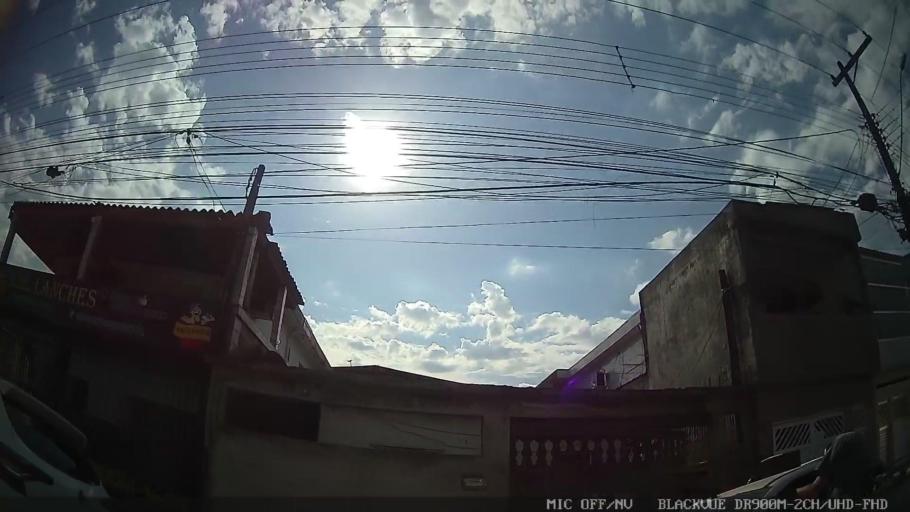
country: BR
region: Sao Paulo
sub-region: Guaruja
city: Guaruja
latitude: -23.9626
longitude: -46.2508
